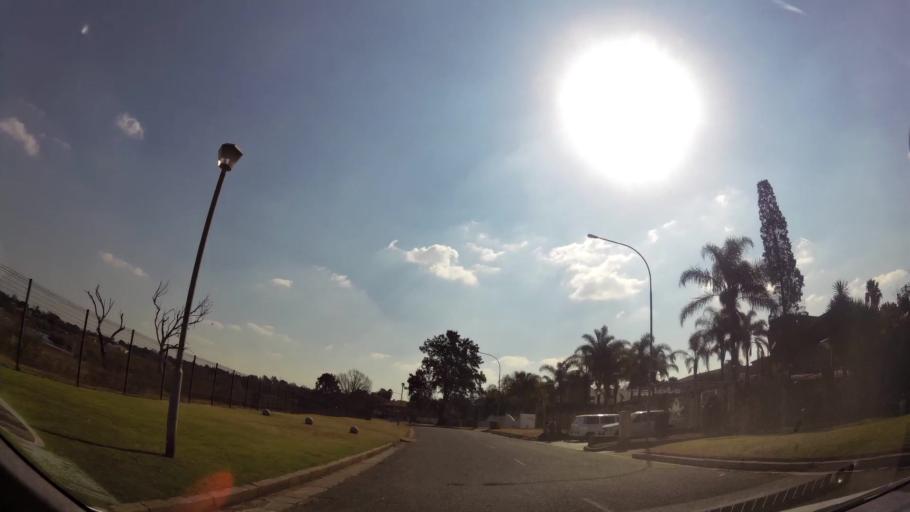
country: ZA
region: Gauteng
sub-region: Ekurhuleni Metropolitan Municipality
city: Benoni
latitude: -26.1911
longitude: 28.2966
